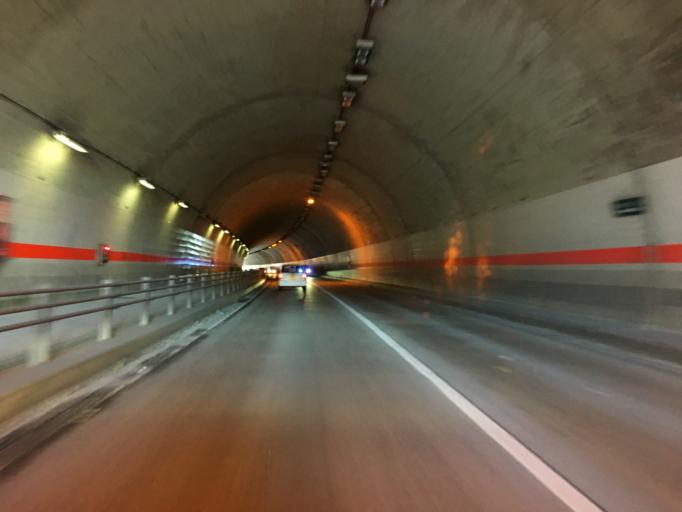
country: JP
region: Fukushima
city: Fukushima-shi
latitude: 37.8326
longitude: 140.4441
